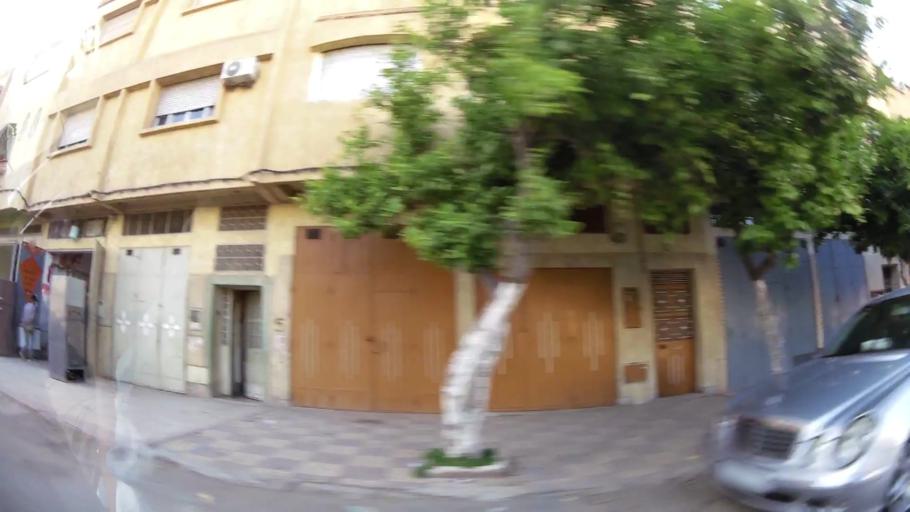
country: MA
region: Oriental
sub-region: Oujda-Angad
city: Oujda
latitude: 34.7038
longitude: -1.8962
